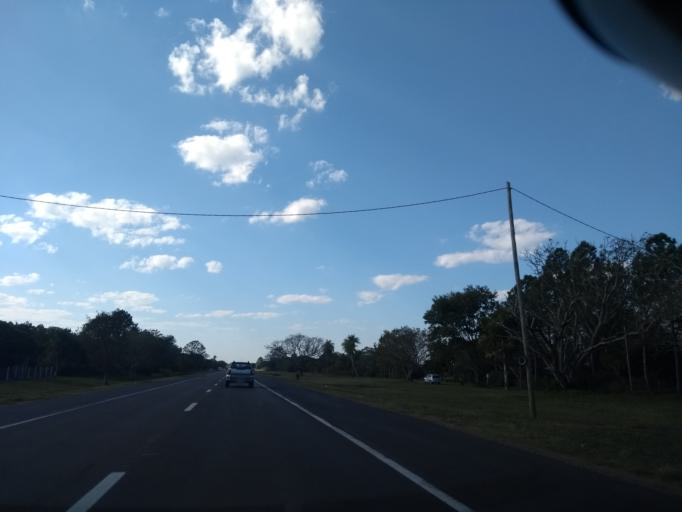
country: AR
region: Corrientes
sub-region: Departamento de San Cosme
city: San Cosme
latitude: -27.3652
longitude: -58.4374
